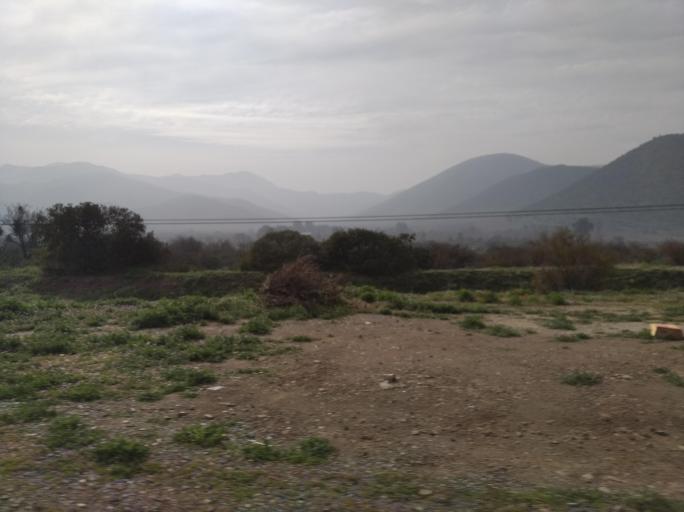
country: CL
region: Santiago Metropolitan
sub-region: Provincia de Chacabuco
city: Lampa
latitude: -33.1324
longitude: -70.9203
